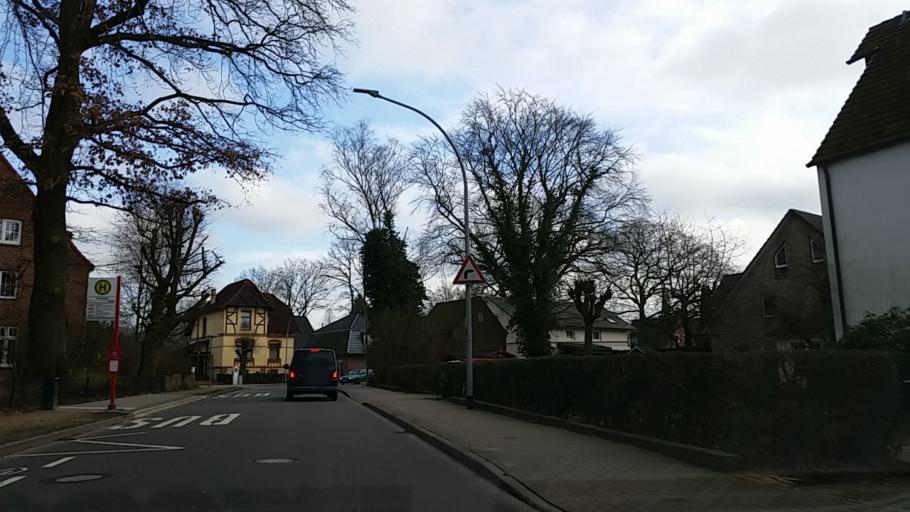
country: DE
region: Schleswig-Holstein
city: Wentorf bei Hamburg
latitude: 53.5018
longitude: 10.2512
